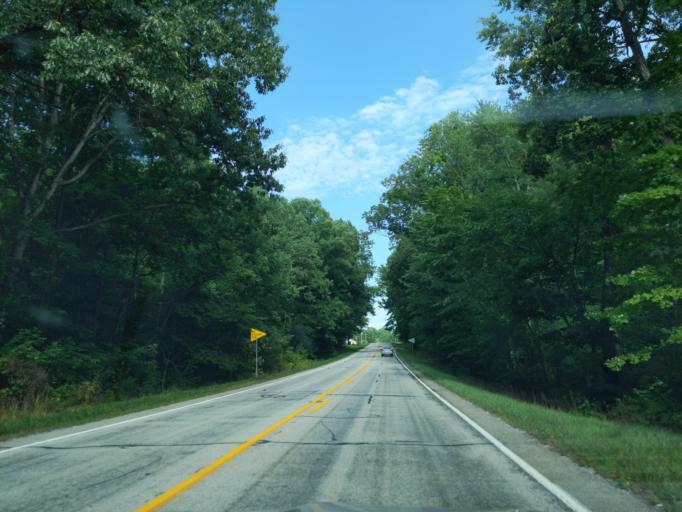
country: US
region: Indiana
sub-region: Ripley County
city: Sunman
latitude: 39.2777
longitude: -85.1241
